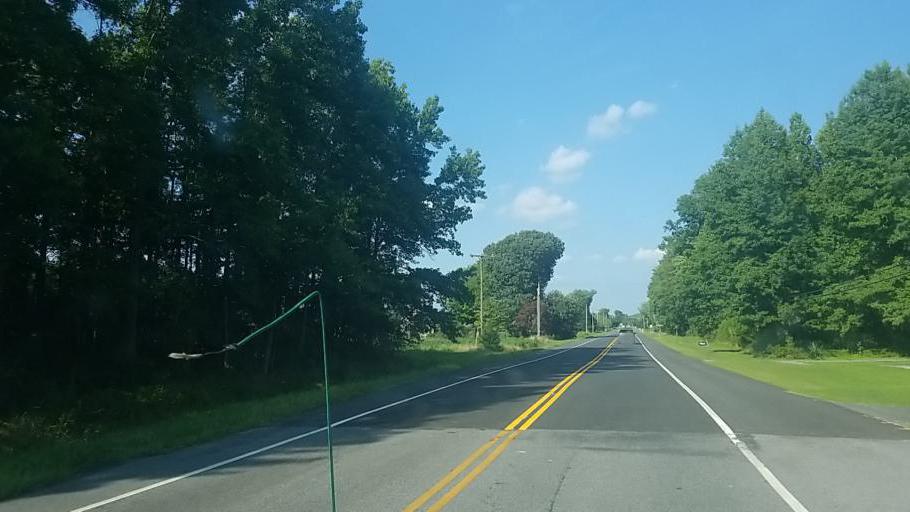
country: US
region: Maryland
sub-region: Worcester County
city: Berlin
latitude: 38.3581
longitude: -75.2125
